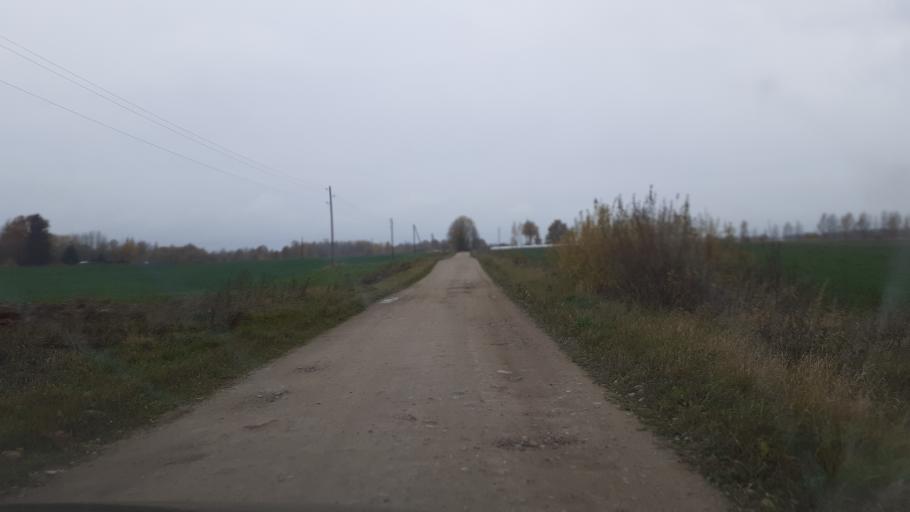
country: LV
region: Saldus Rajons
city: Saldus
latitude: 56.8634
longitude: 22.3506
